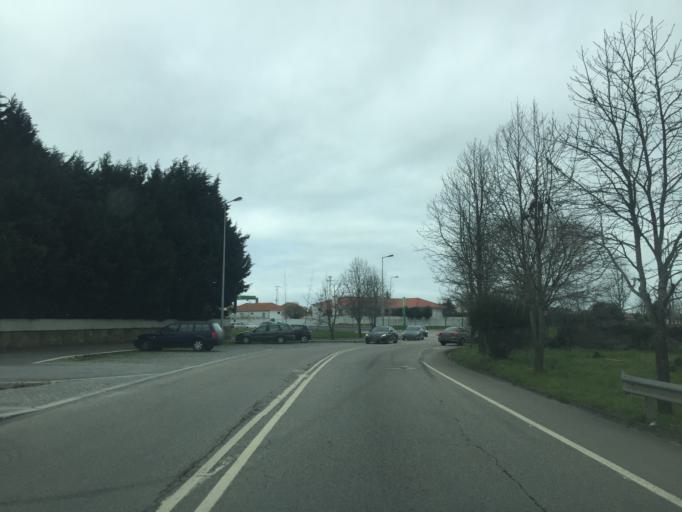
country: PT
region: Porto
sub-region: Matosinhos
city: Santa Cruz do Bispo
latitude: 41.2270
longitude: -8.6974
